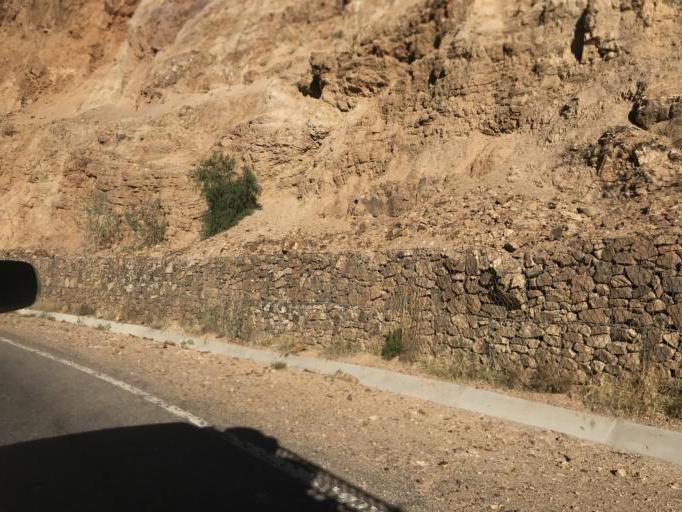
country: BO
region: Chuquisaca
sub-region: Provincia Oropeza
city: Yotala
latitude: -19.1449
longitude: -65.2012
